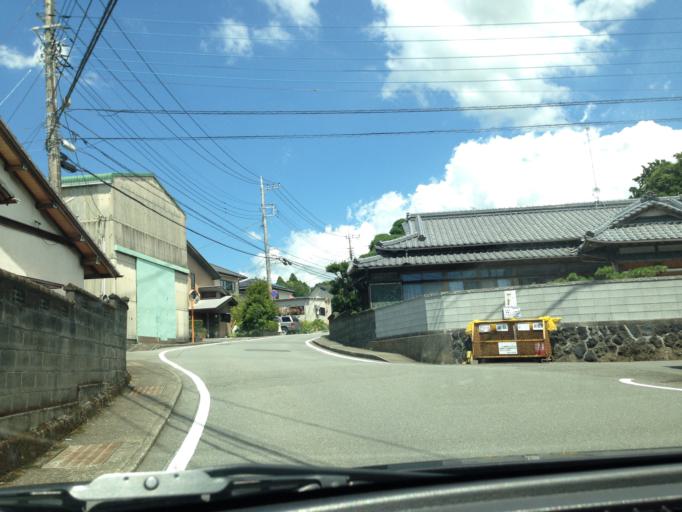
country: JP
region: Shizuoka
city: Fuji
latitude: 35.1931
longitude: 138.7127
